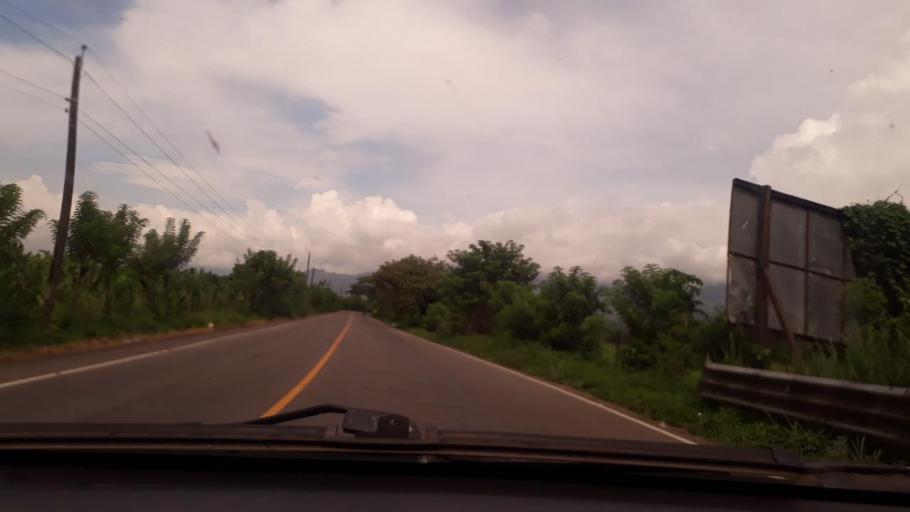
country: HN
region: Cortes
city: Potrerillos
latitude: 15.6070
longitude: -88.3919
